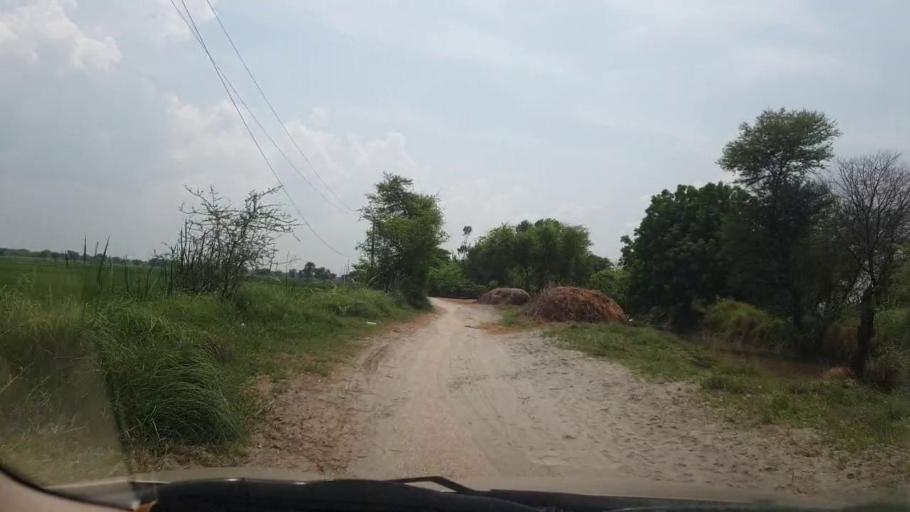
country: PK
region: Sindh
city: Larkana
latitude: 27.5950
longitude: 68.1229
